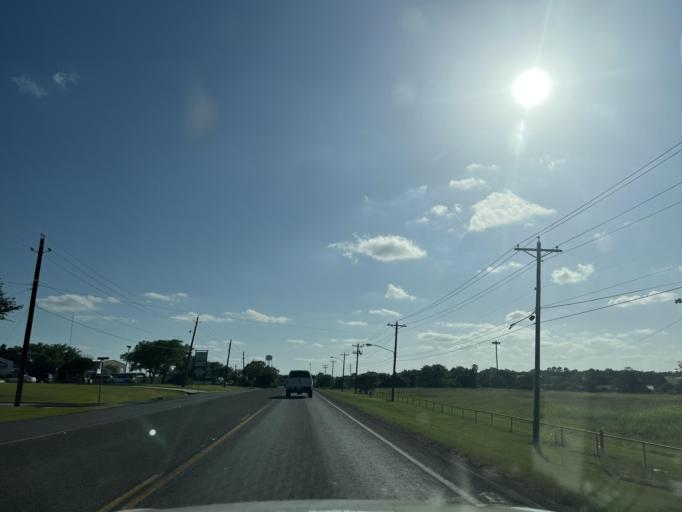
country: US
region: Texas
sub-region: Washington County
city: Brenham
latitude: 30.1784
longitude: -96.3908
